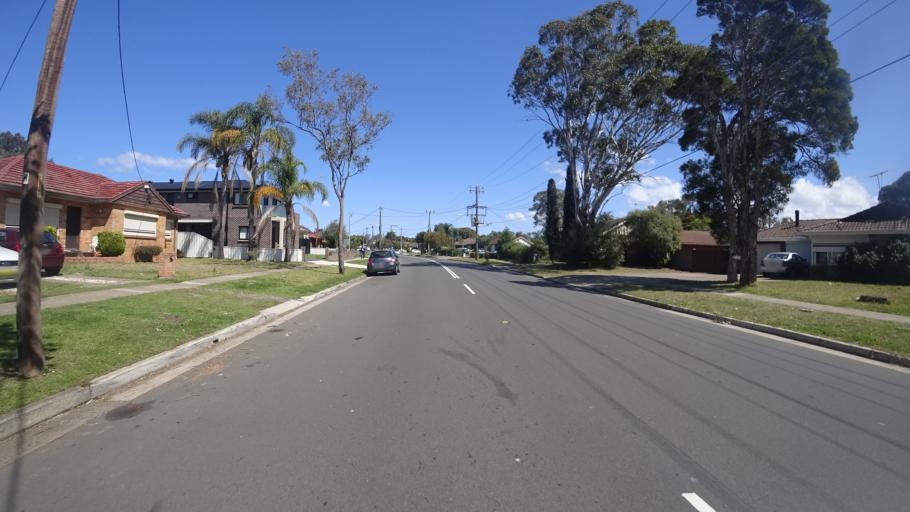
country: AU
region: New South Wales
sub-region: Liverpool
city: Miller
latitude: -33.9272
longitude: 150.8982
